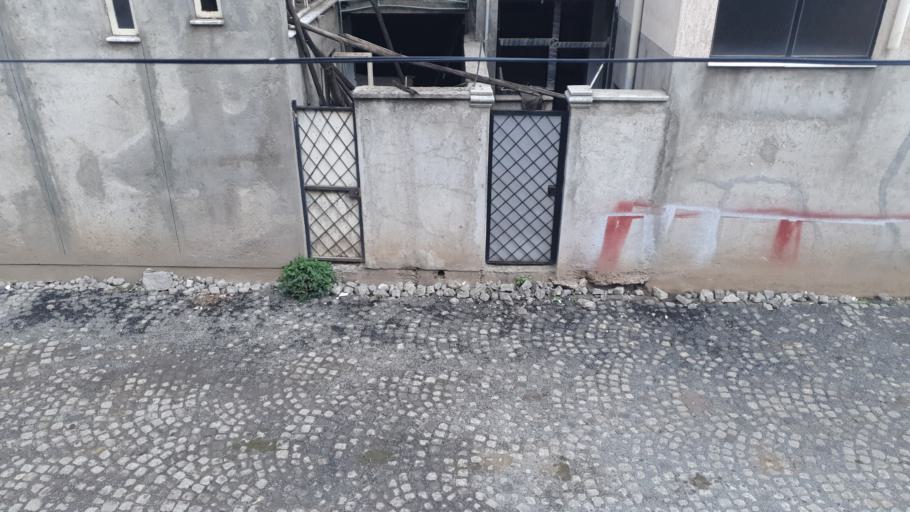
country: ET
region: Adis Abeba
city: Addis Ababa
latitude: 8.9579
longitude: 38.7227
